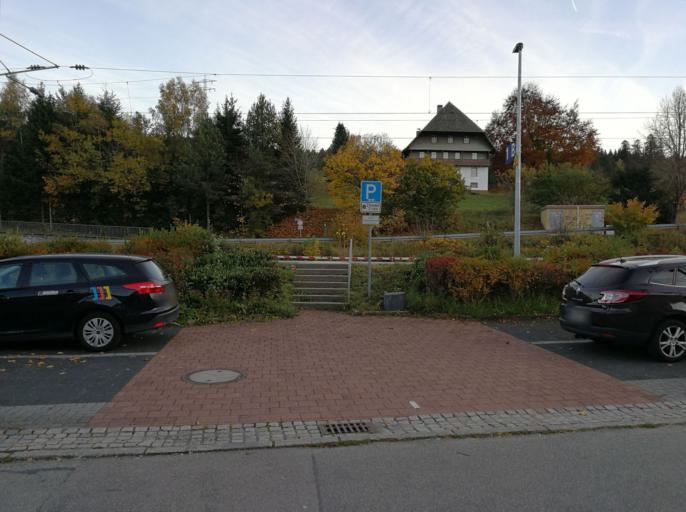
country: DE
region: Baden-Wuerttemberg
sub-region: Freiburg Region
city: Sankt Georgen im Schwarzwald
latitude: 48.1238
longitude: 8.3411
